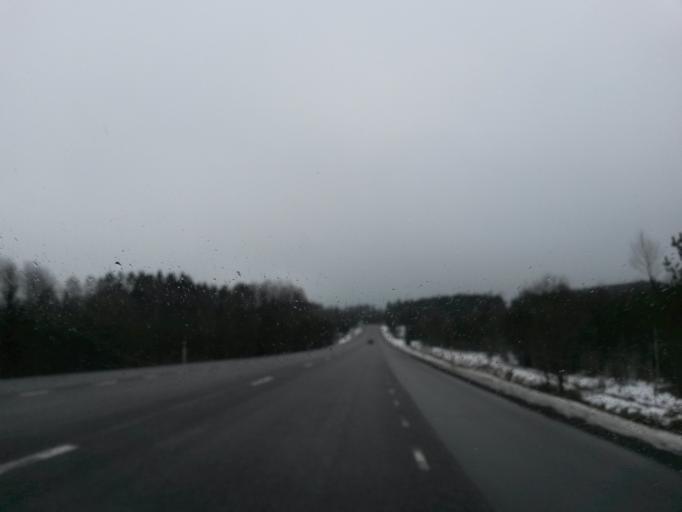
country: SE
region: Vaestra Goetaland
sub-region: Boras Kommun
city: Viskafors
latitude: 57.6002
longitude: 12.8722
